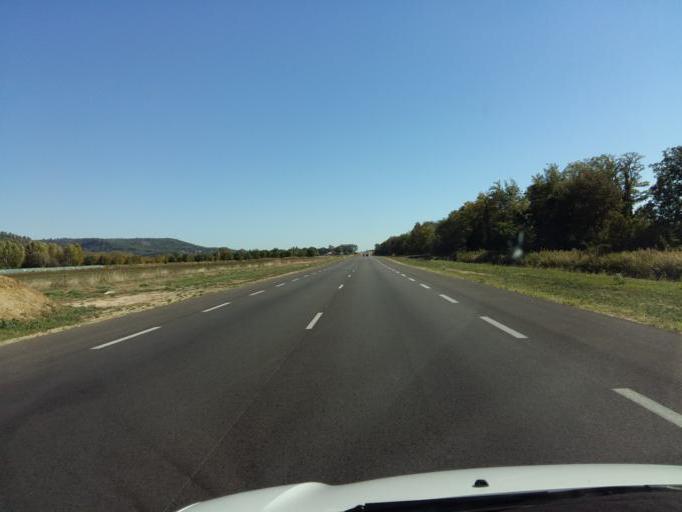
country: FR
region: Provence-Alpes-Cote d'Azur
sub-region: Departement du Vaucluse
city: Cadenet
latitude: 43.7179
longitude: 5.3988
